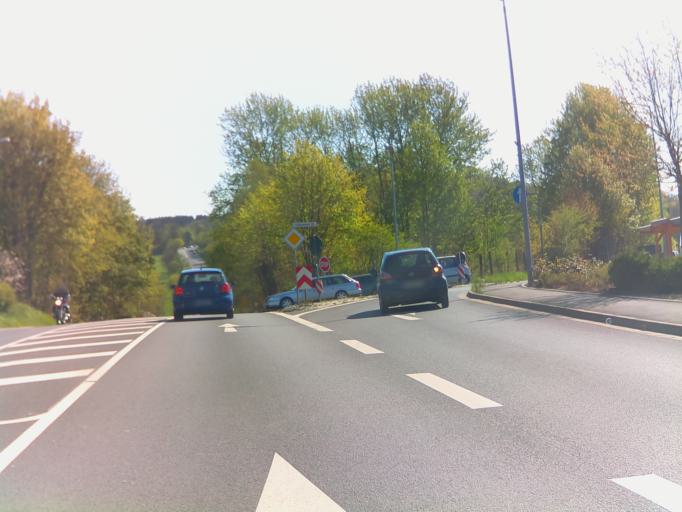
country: DE
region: Saxony
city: Neuensalz
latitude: 50.4968
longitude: 12.1782
